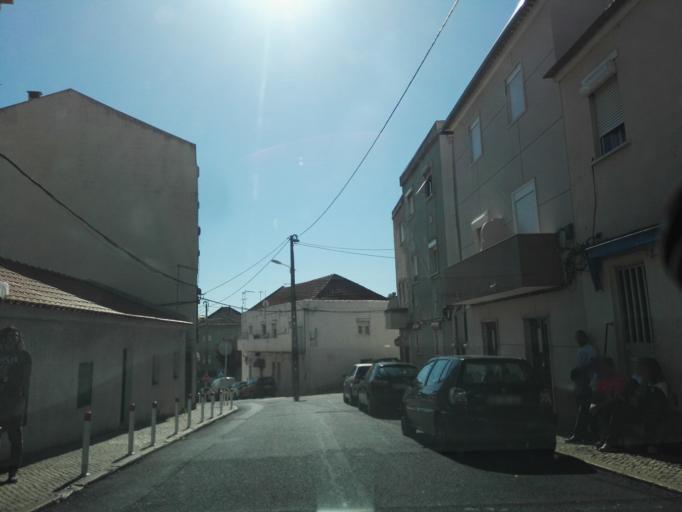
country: PT
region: Lisbon
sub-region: Loures
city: Sacavem
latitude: 38.7906
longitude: -9.1201
